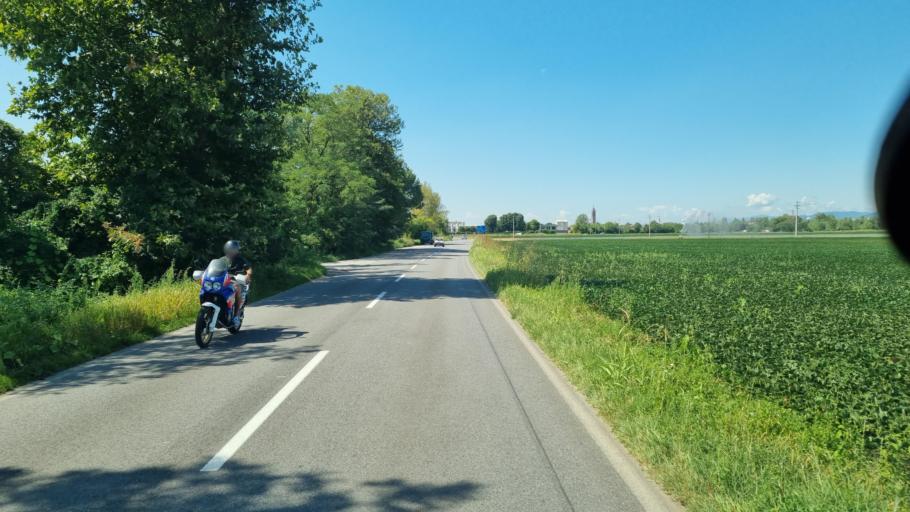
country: IT
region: Lombardy
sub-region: Provincia di Bergamo
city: Levate
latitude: 45.6195
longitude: 9.6419
